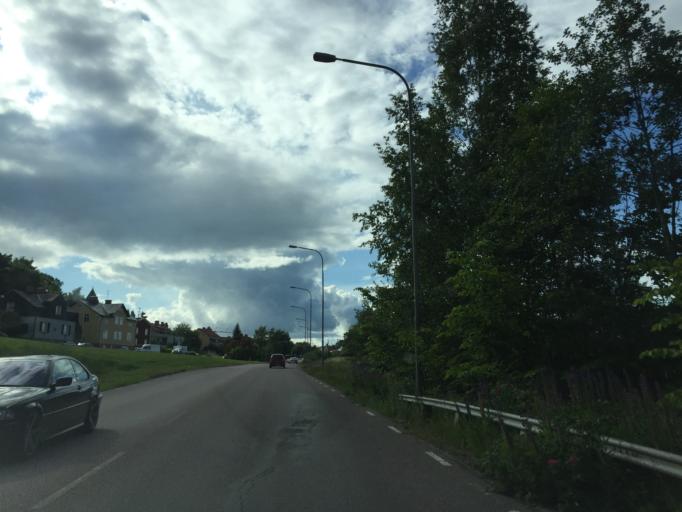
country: SE
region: Vaestmanland
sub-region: Vasteras
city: Vasteras
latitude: 59.6151
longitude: 16.5301
